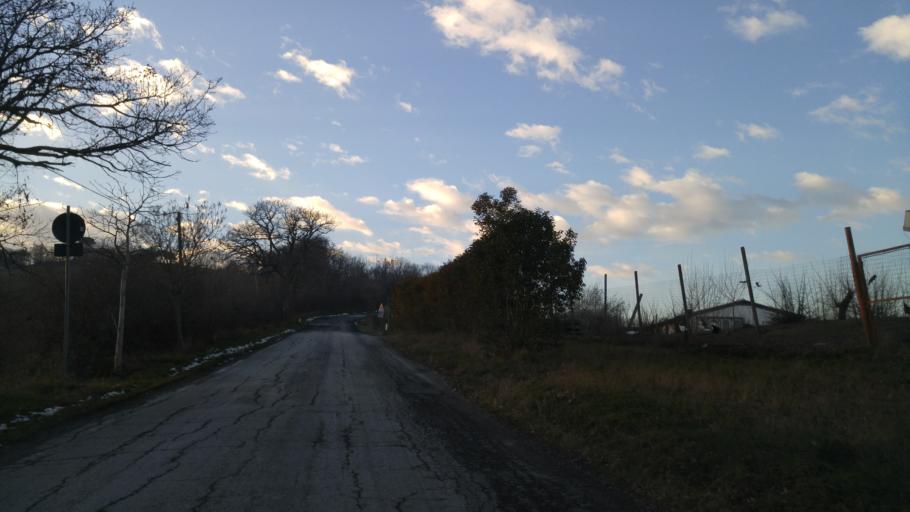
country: IT
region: The Marches
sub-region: Provincia di Pesaro e Urbino
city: Monte Porzio
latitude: 43.6935
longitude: 13.0390
